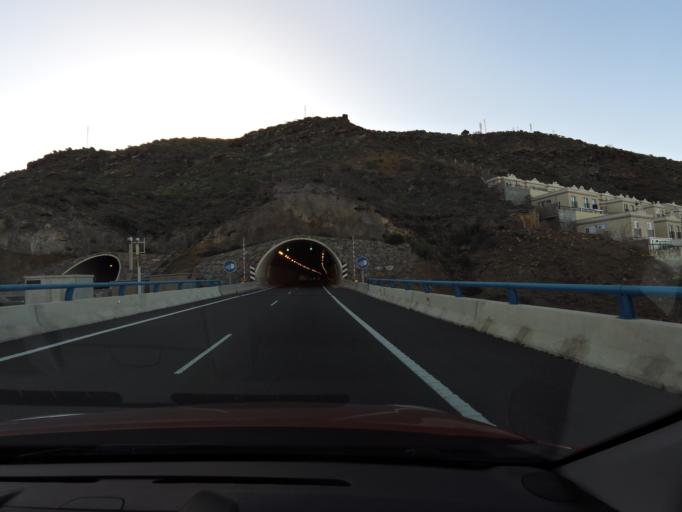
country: ES
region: Canary Islands
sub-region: Provincia de Las Palmas
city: Puerto Rico
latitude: 27.7967
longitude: -15.7014
